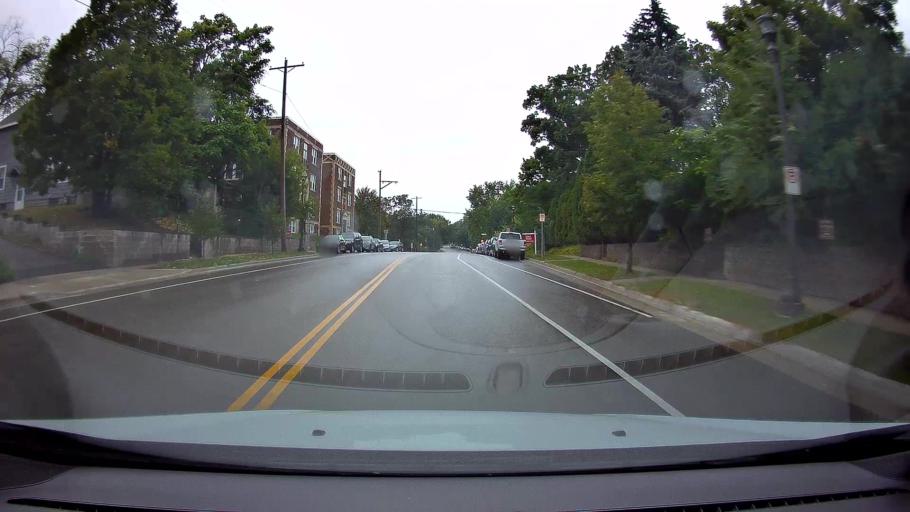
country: US
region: Minnesota
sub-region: Ramsey County
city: Lauderdale
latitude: 44.9778
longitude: -93.1895
